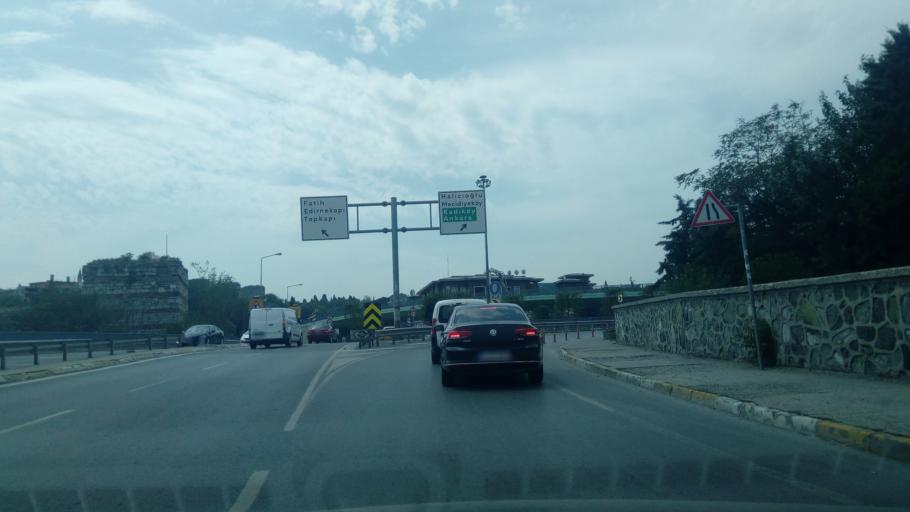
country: TR
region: Istanbul
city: Istanbul
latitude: 41.0398
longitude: 28.9397
